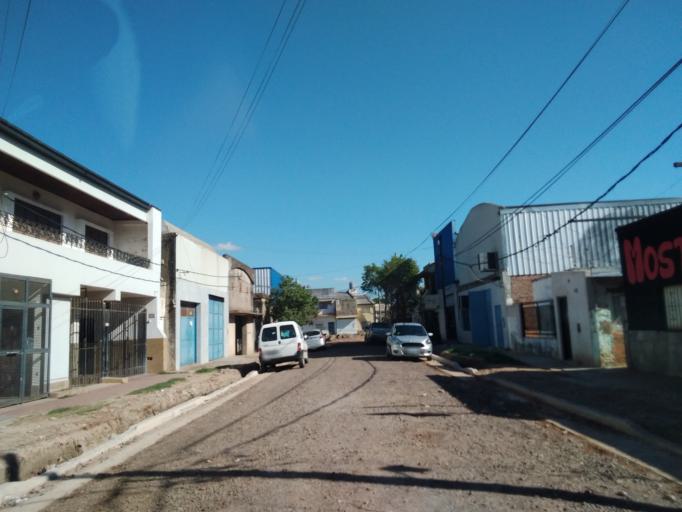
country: AR
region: Corrientes
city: Corrientes
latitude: -27.4790
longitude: -58.8136
